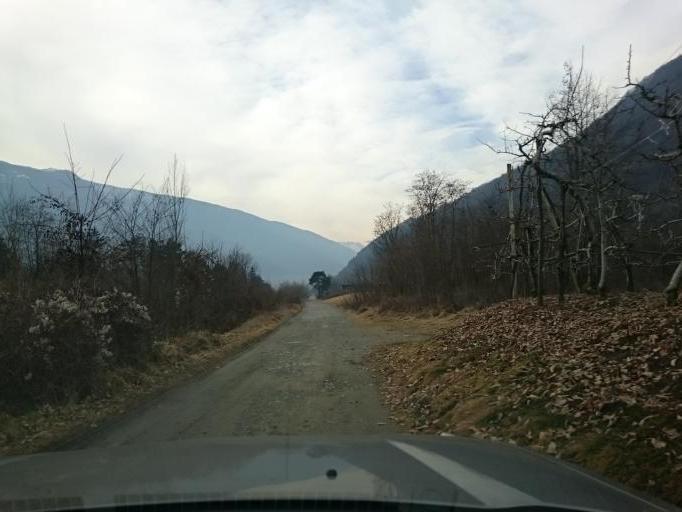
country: IT
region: Lombardy
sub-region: Provincia di Sondrio
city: Vervio
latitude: 46.2556
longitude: 10.2460
